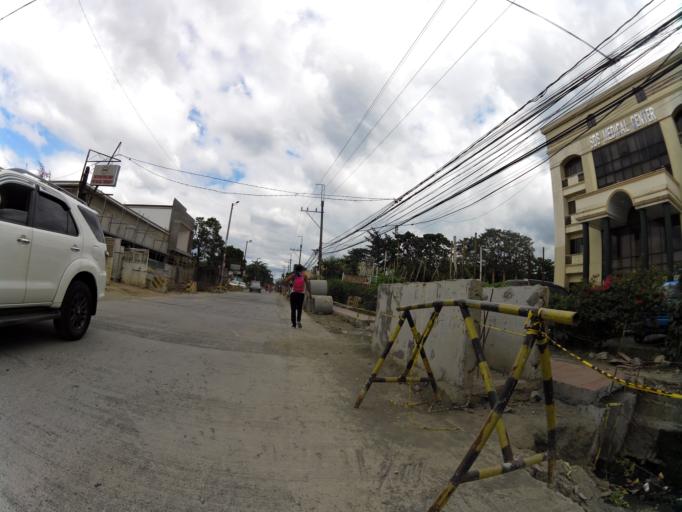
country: PH
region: Calabarzon
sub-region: Province of Rizal
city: Antipolo
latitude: 14.6393
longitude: 121.1097
